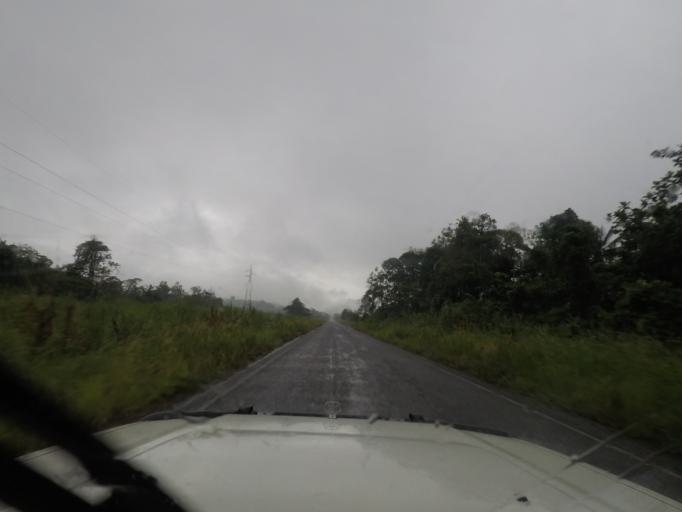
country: PG
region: Madang
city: Madang
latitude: -5.3955
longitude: 145.6725
